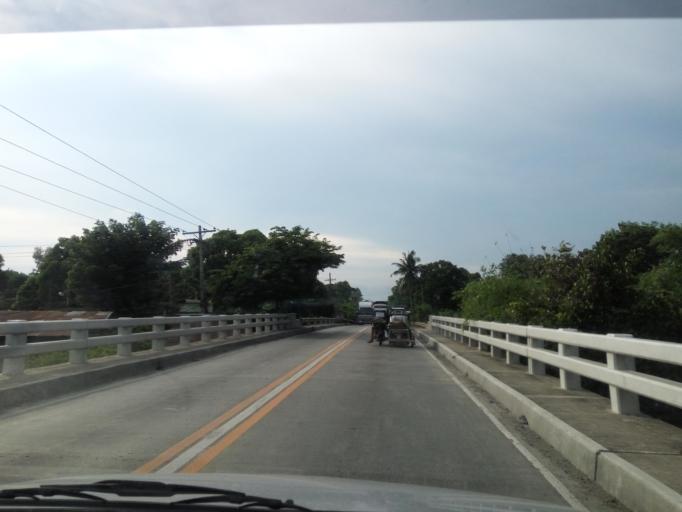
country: PH
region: Ilocos
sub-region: Province of Pangasinan
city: Binalonan
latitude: 16.0877
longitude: 120.5785
